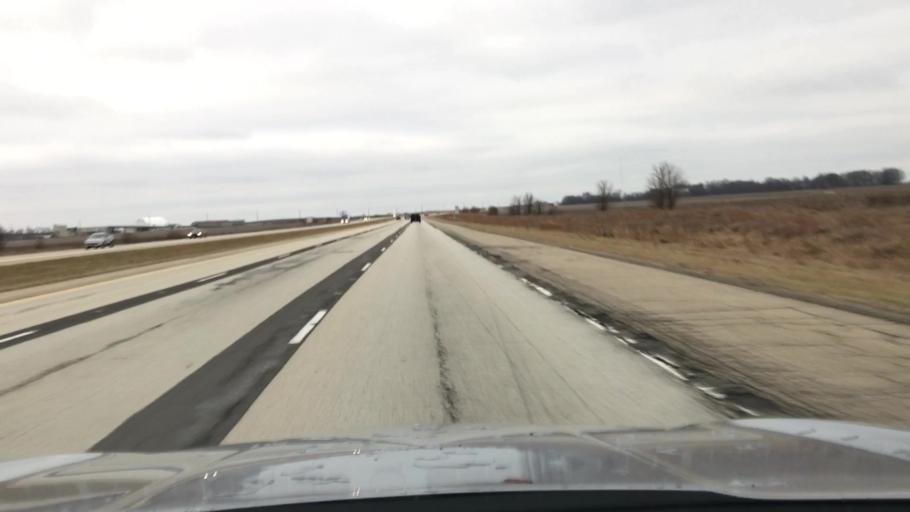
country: US
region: Illinois
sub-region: Sangamon County
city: Williamsville
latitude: 40.0129
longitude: -89.4996
